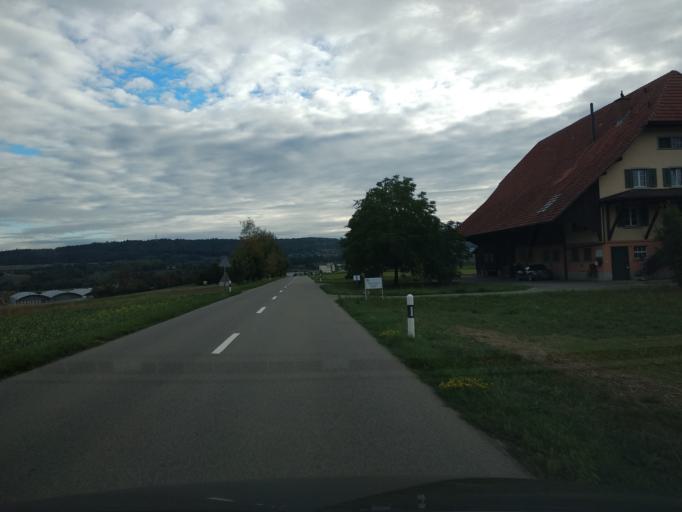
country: CH
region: Thurgau
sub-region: Frauenfeld District
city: Diessenhofen
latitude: 47.6806
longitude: 8.7287
